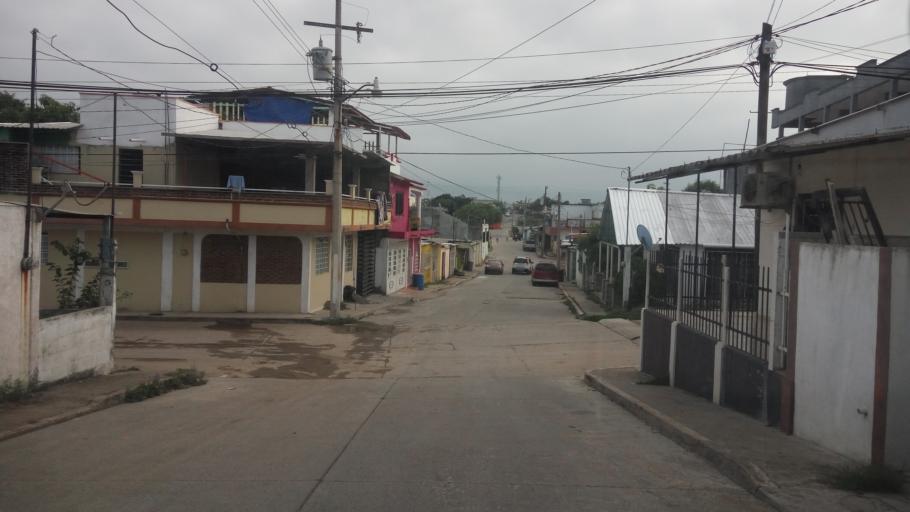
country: MX
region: Chiapas
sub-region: Reforma
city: El Carmen (El Limon)
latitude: 17.8572
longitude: -93.1538
